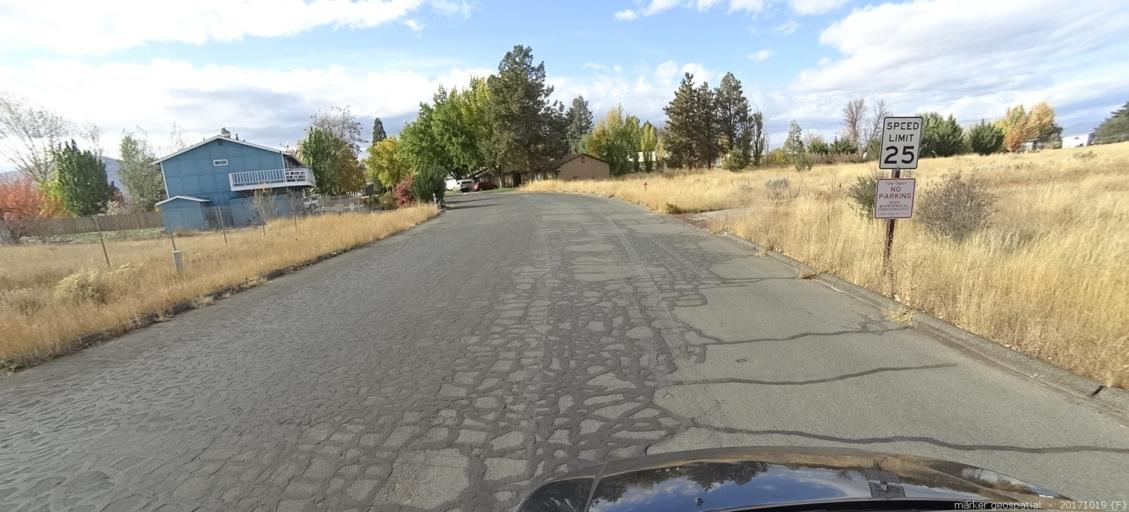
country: US
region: California
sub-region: Shasta County
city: Burney
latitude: 41.0275
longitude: -121.4233
